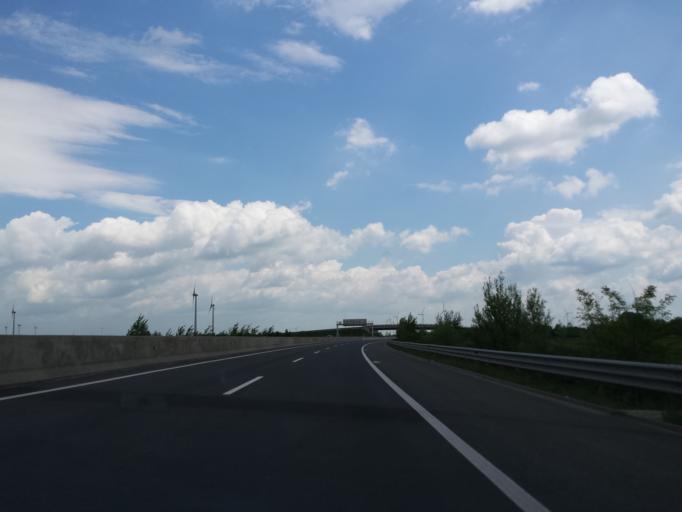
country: AT
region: Burgenland
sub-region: Politischer Bezirk Neusiedl am See
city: Parndorf
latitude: 48.0270
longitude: 16.8517
